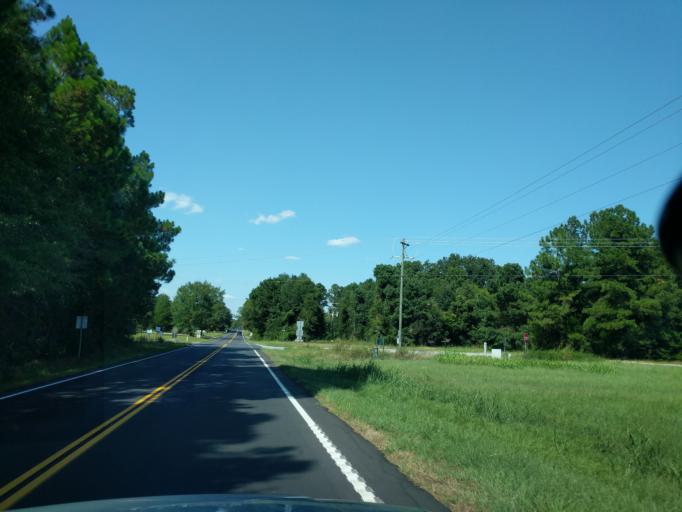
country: US
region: South Carolina
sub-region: Lexington County
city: Batesburg-Leesville
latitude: 33.9390
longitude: -81.5352
